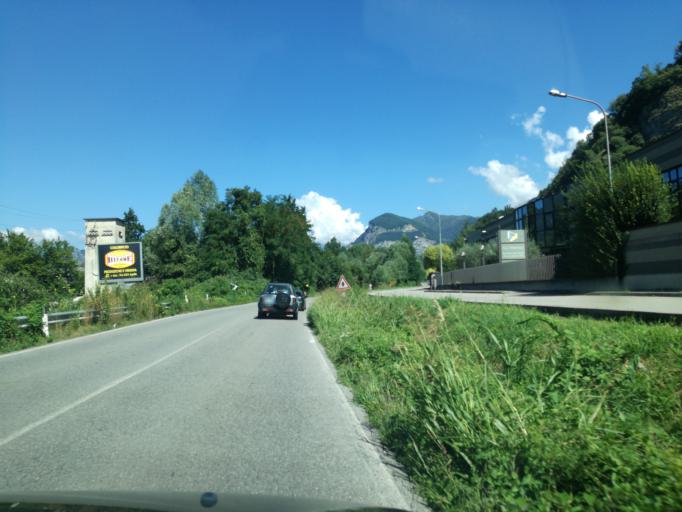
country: IT
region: Lombardy
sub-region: Provincia di Lecco
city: Monte Marenzo
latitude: 45.7712
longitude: 9.4435
